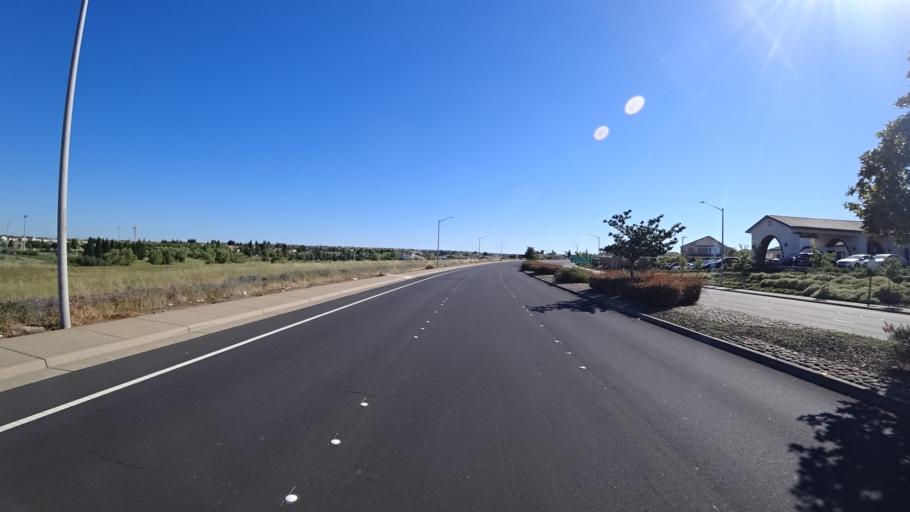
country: US
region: California
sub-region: Placer County
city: Rocklin
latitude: 38.8172
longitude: -121.2837
